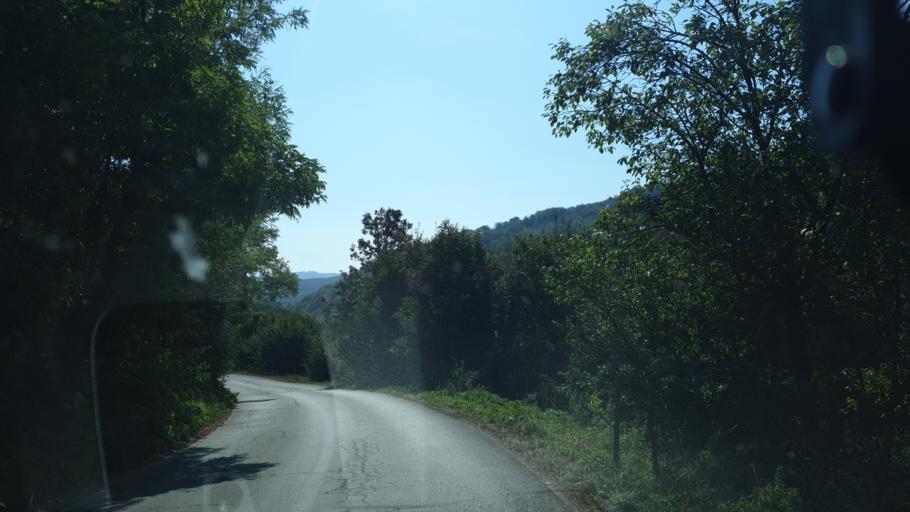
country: RS
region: Central Serbia
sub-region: Zlatiborski Okrug
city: Cajetina
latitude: 43.7139
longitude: 19.8332
